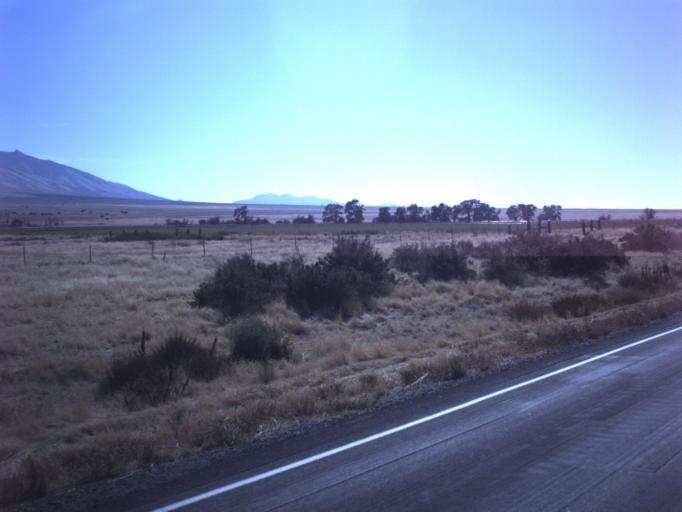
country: US
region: Utah
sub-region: Tooele County
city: Grantsville
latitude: 40.4607
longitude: -112.7473
